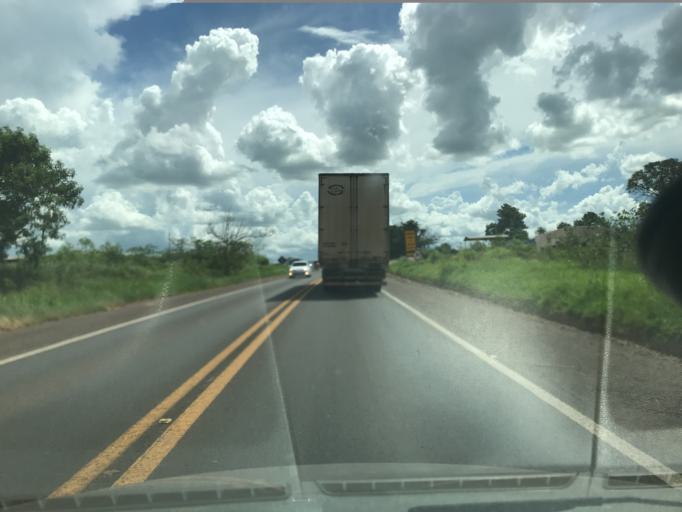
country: BR
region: Parana
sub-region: Cruzeiro Do Oeste
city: Cruzeiro do Oeste
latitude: -23.7983
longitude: -53.0526
